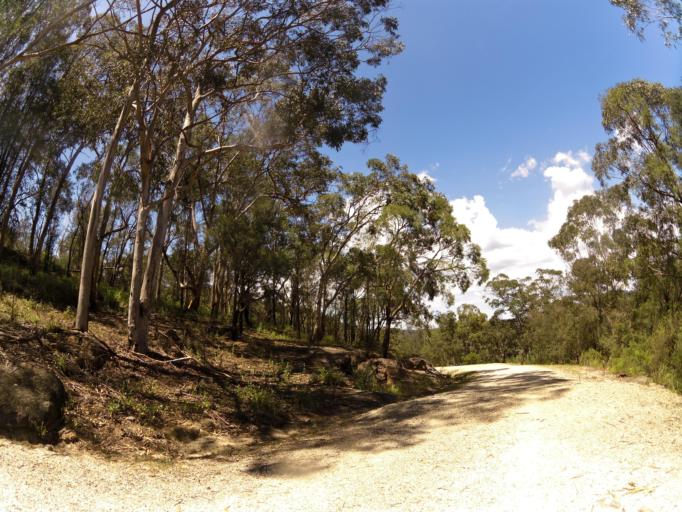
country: AU
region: New South Wales
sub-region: Hornsby Shire
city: Glenorie
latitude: -33.3666
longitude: 150.9865
